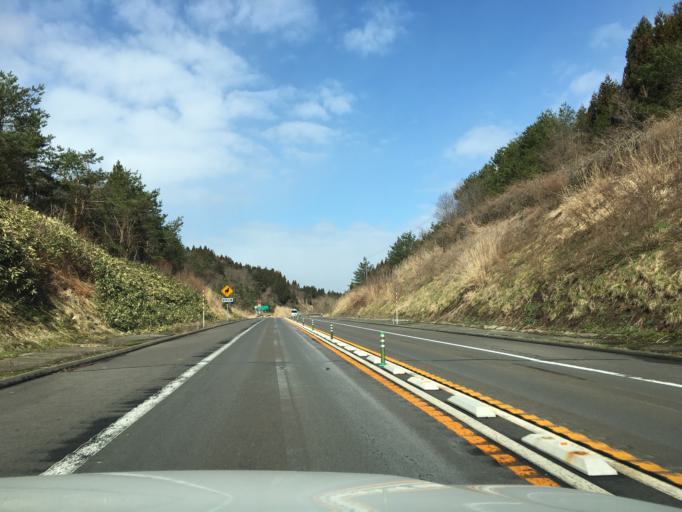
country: JP
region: Akita
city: Akita
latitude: 39.7636
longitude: 140.1266
